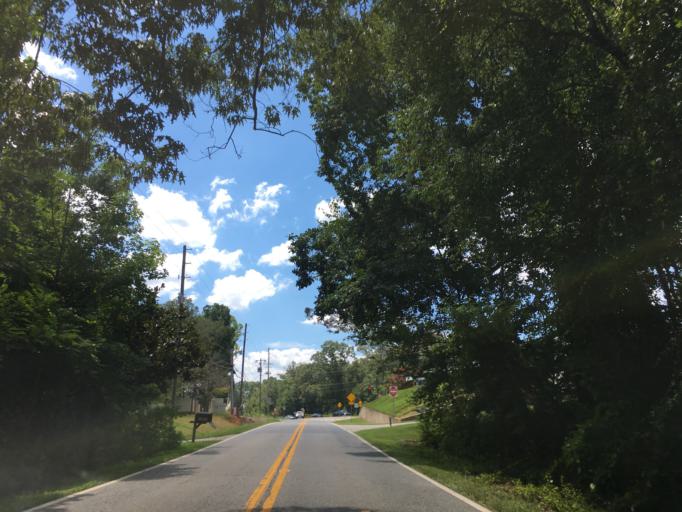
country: US
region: Georgia
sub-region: Fulton County
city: Roswell
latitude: 34.0919
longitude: -84.3615
